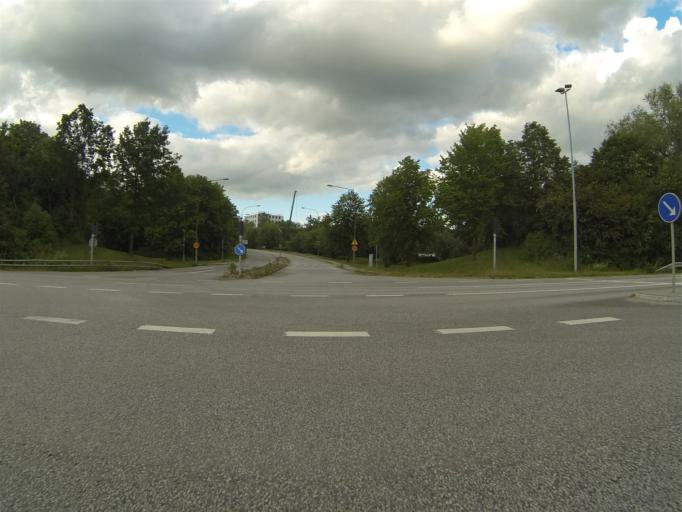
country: SE
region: Skane
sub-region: Lunds Kommun
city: Lund
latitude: 55.6923
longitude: 13.2409
